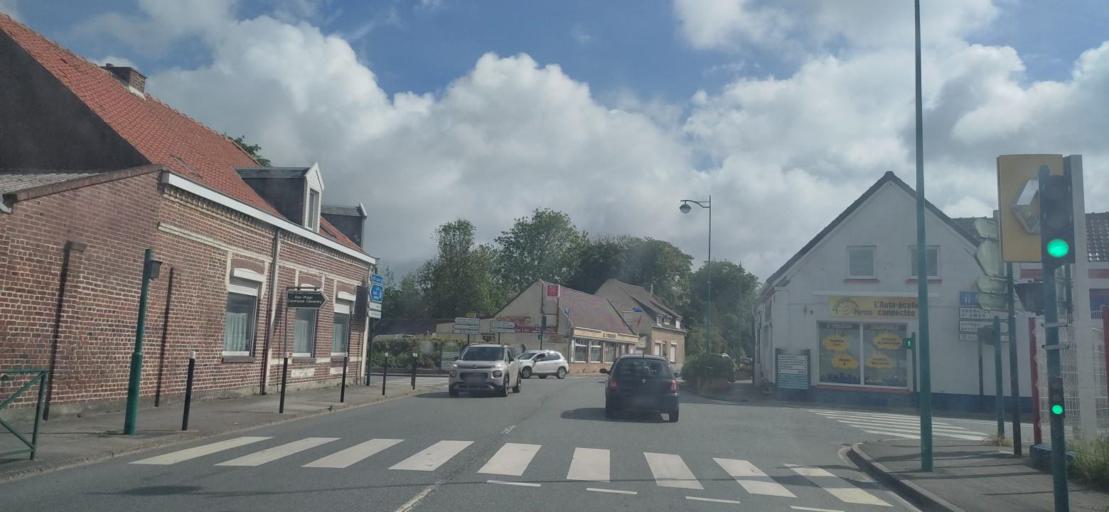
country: FR
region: Nord-Pas-de-Calais
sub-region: Departement du Pas-de-Calais
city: Oye-Plage
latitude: 50.9777
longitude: 2.0389
